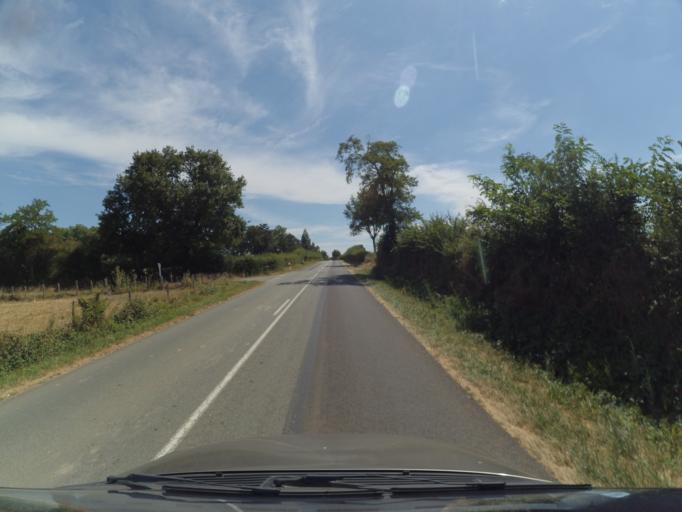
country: FR
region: Poitou-Charentes
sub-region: Departement de la Vienne
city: Usson-du-Poitou
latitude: 46.3093
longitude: 0.4962
